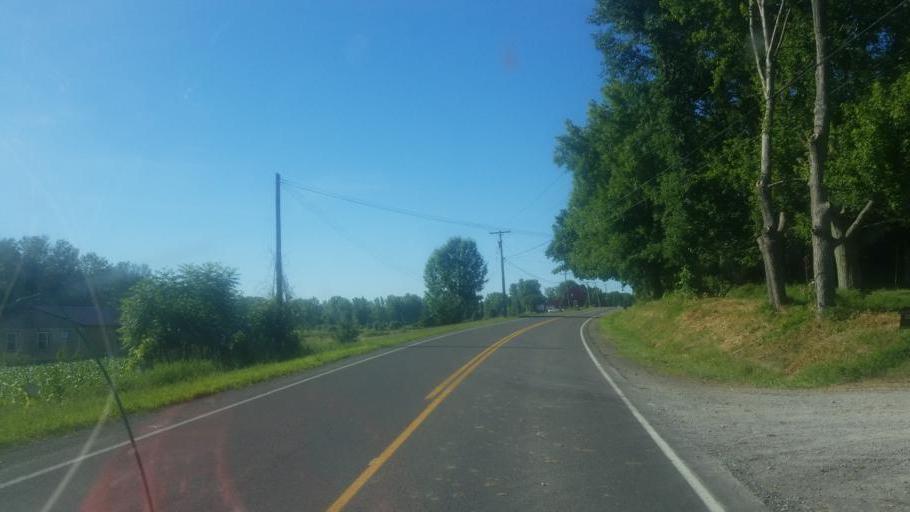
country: US
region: New York
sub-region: Ontario County
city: Phelps
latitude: 42.9383
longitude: -77.0694
